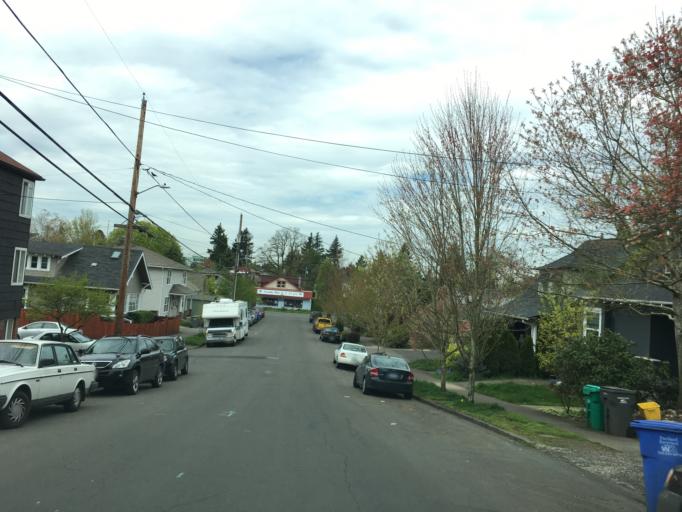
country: US
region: Oregon
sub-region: Multnomah County
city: Lents
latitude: 45.5255
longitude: -122.6008
